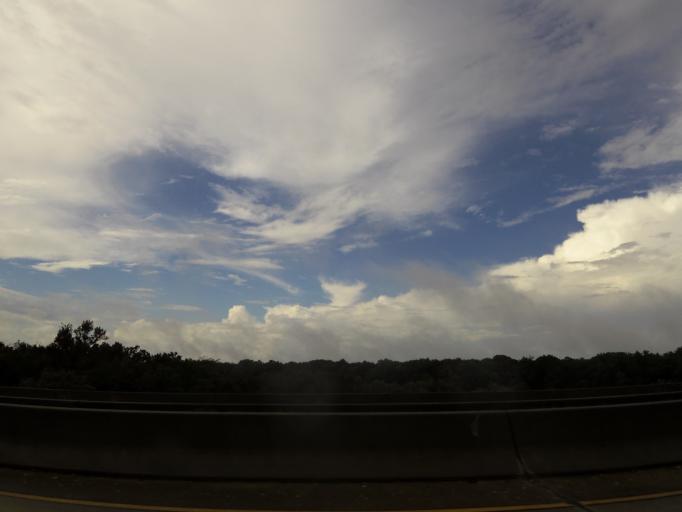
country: US
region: Georgia
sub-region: Wayne County
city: Jesup
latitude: 31.6661
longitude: -81.8399
